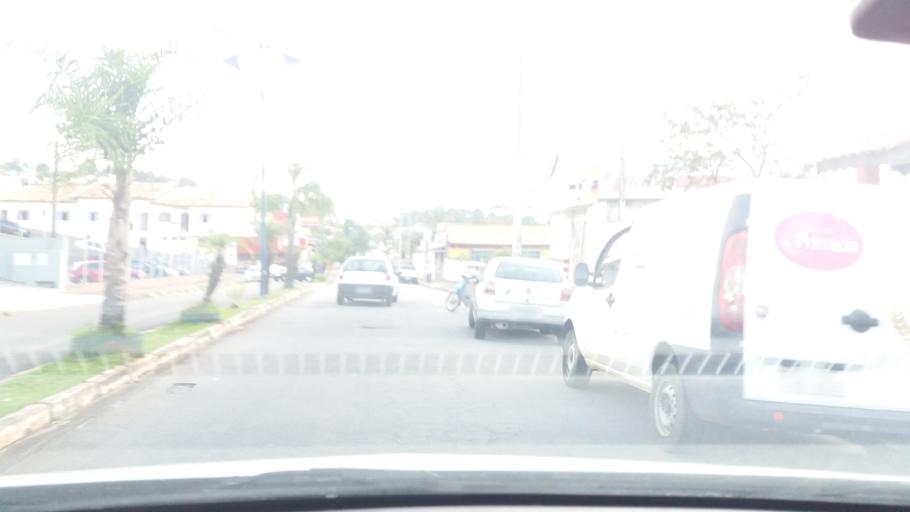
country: BR
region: Sao Paulo
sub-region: Bom Jesus Dos Perdoes
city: Bom Jesus dos Perdoes
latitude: -23.1407
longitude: -46.4674
